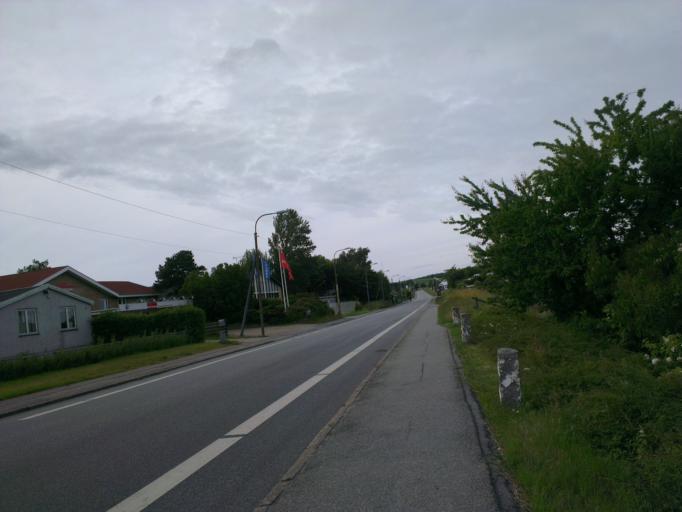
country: DK
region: Capital Region
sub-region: Frederikssund Kommune
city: Skibby
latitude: 55.7550
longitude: 11.9589
